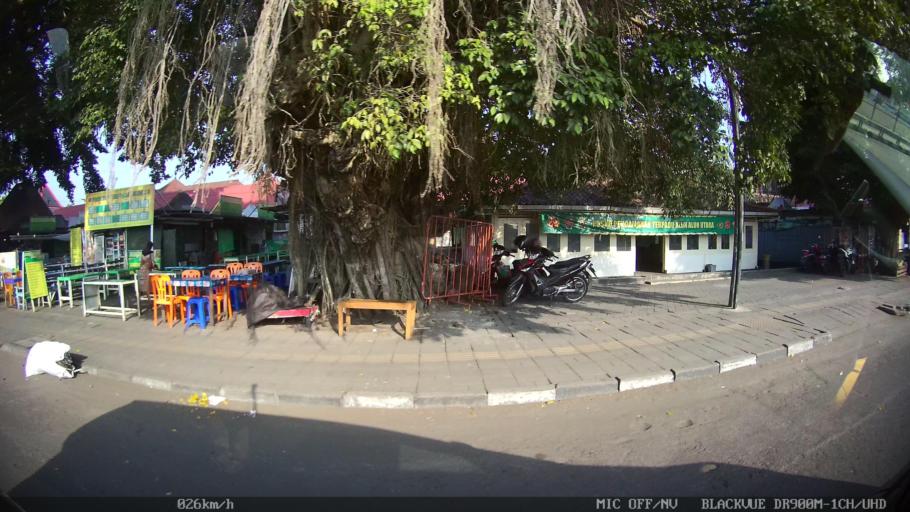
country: ID
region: Daerah Istimewa Yogyakarta
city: Yogyakarta
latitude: -7.8037
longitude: 110.3632
